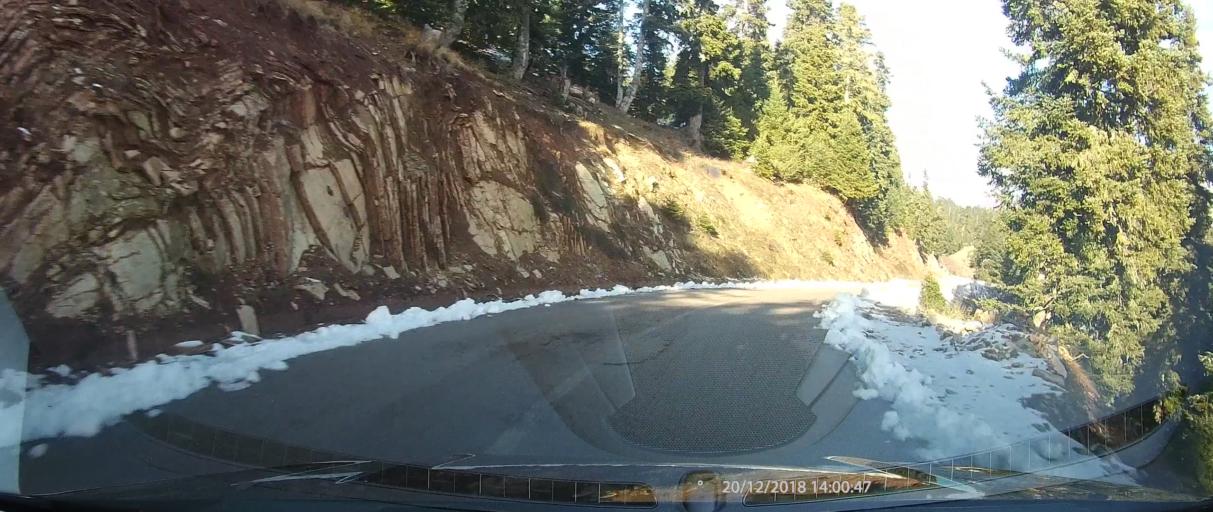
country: GR
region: West Greece
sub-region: Nomos Aitolias kai Akarnanias
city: Thermo
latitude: 38.7271
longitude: 21.6277
